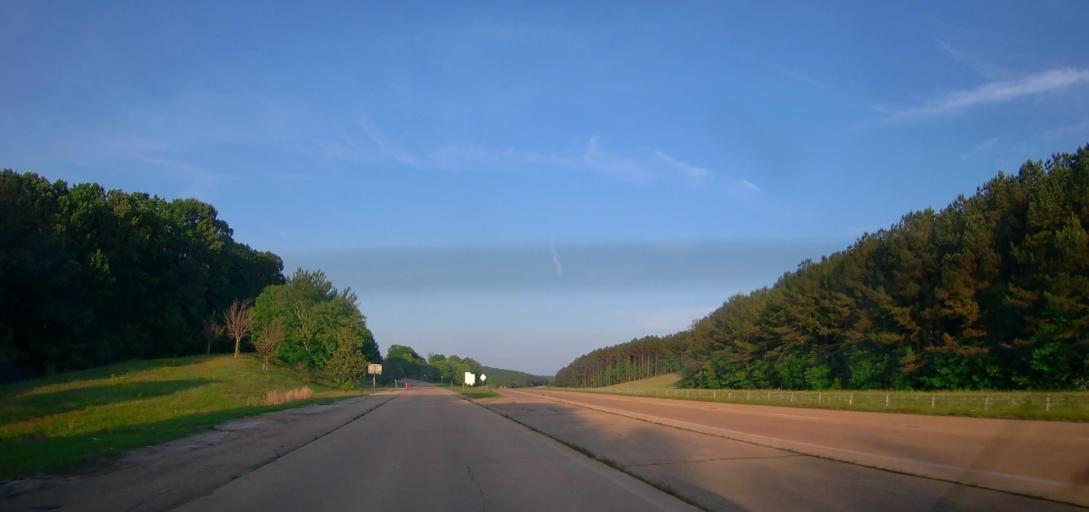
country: US
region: Mississippi
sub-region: Itawamba County
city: Fulton
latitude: 34.2207
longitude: -88.2379
